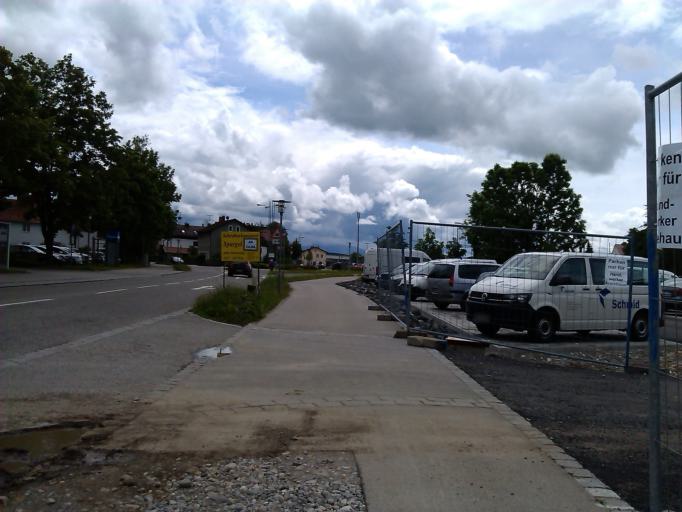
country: DE
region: Bavaria
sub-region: Swabia
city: Marktoberdorf
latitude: 47.7825
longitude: 10.6152
